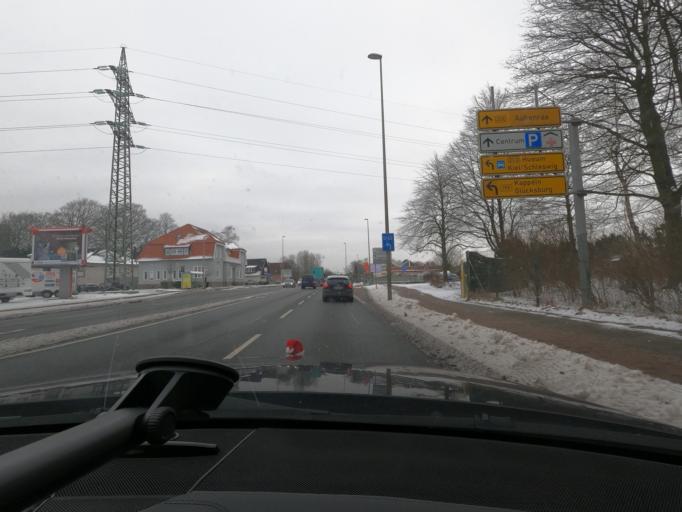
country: DE
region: Schleswig-Holstein
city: Harrislee
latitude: 54.7756
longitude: 9.4062
